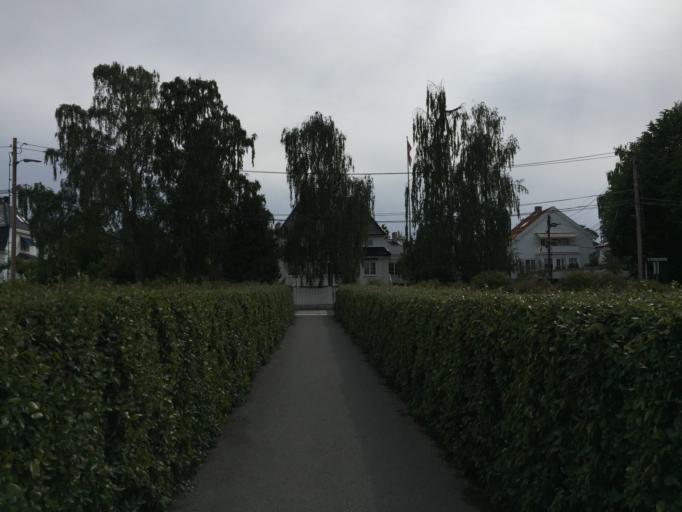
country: NO
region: Oslo
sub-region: Oslo
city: Sjolyststranda
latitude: 59.9044
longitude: 10.6851
